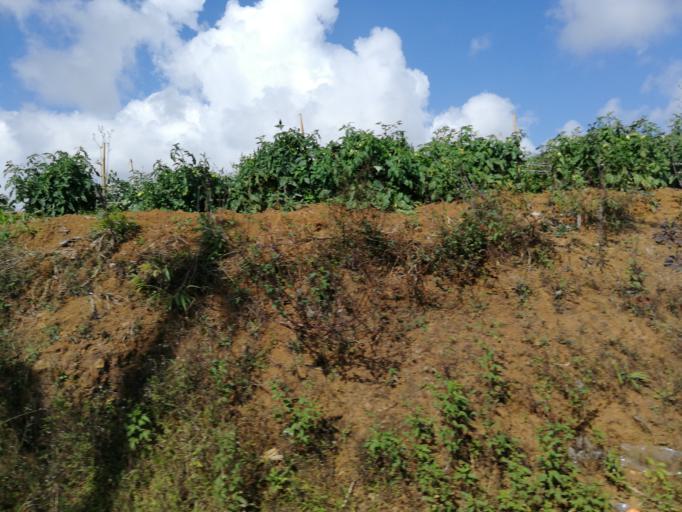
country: MU
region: Pamplemousses
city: Creve Coeur
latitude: -20.2078
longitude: 57.5580
